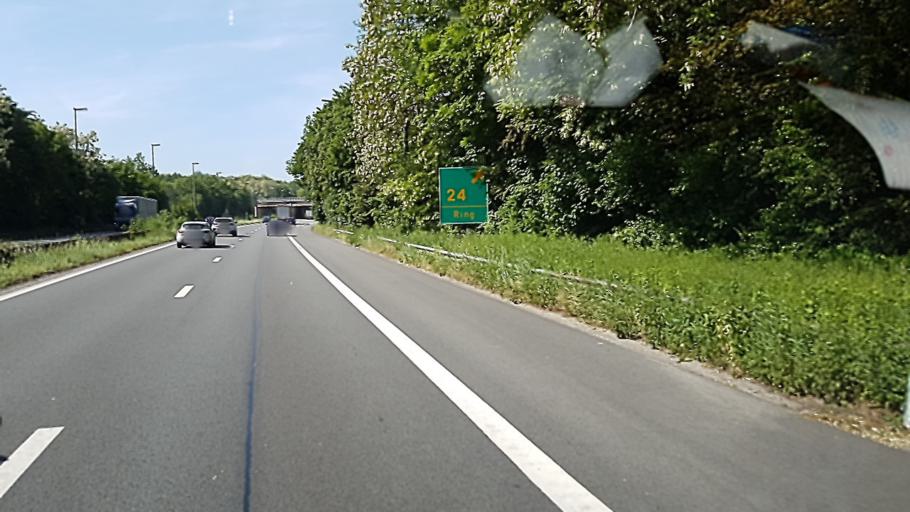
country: BE
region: Wallonia
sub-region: Province du Brabant Wallon
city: Braine-l'Alleud
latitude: 50.6675
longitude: 4.3873
